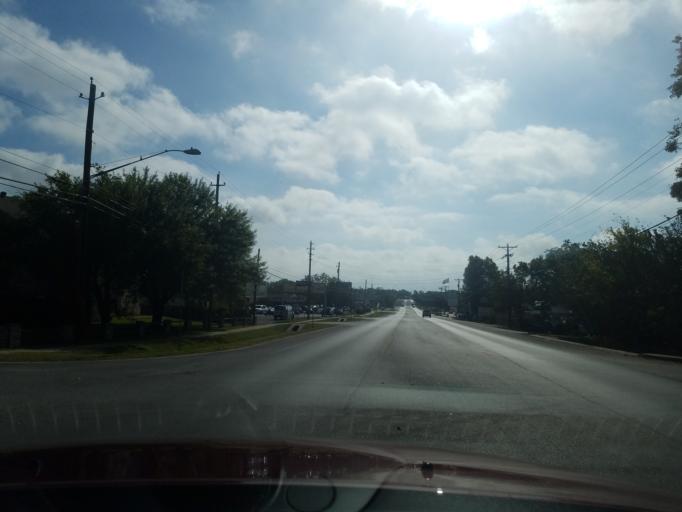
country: US
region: Texas
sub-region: Williamson County
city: Jollyville
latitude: 30.4466
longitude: -97.7802
